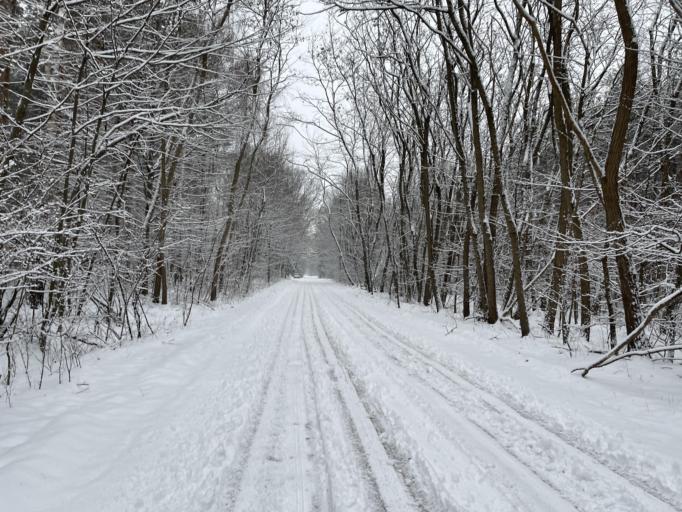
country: PL
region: Masovian Voivodeship
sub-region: Powiat zyrardowski
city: Guzow
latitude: 52.0474
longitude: 20.2728
